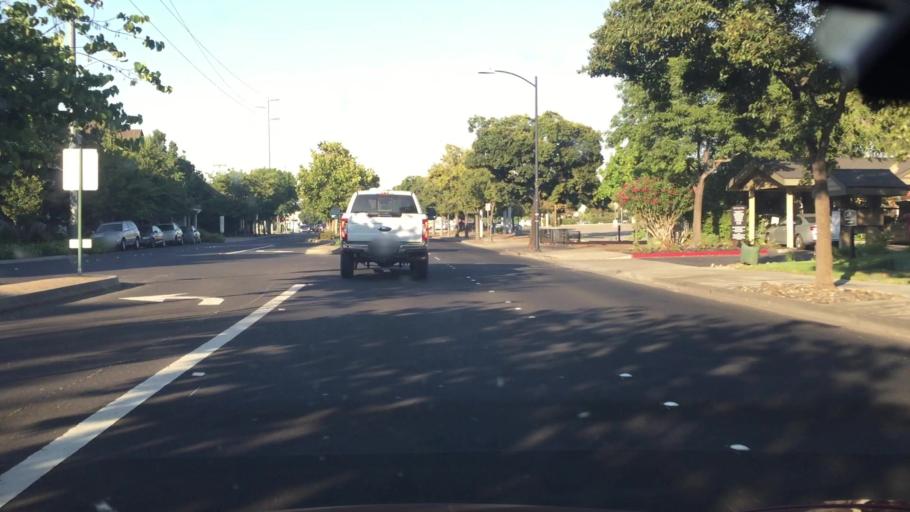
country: US
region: California
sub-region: Alameda County
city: Livermore
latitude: 37.6820
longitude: -121.7737
